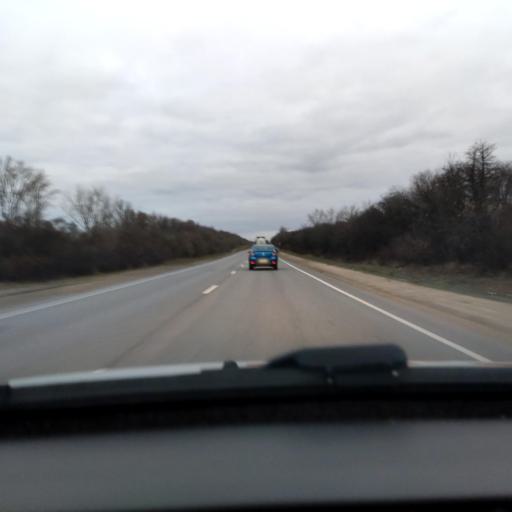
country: RU
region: Lipetsk
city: Borinskoye
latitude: 52.4364
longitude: 39.2744
